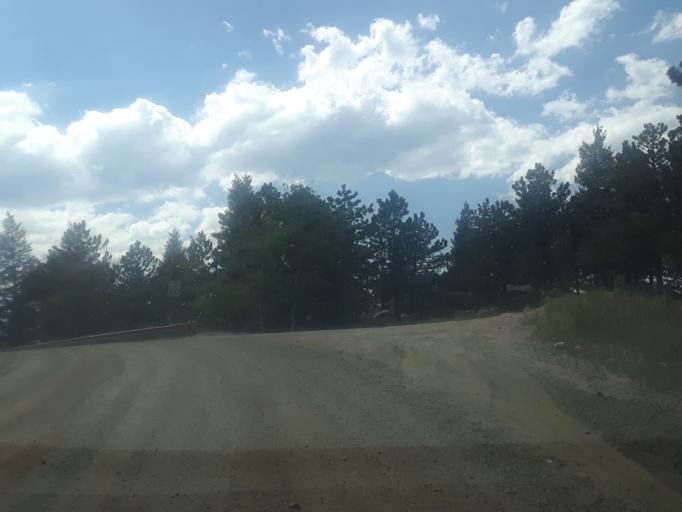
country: US
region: Colorado
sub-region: Boulder County
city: Boulder
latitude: 40.0716
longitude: -105.3871
